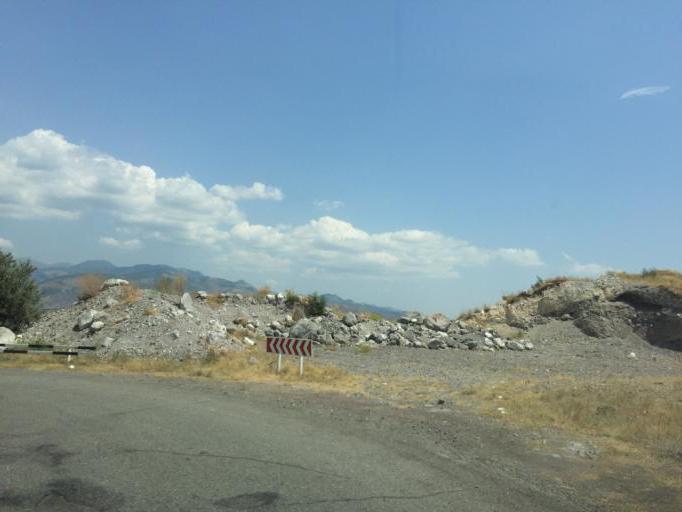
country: AZ
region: Lacin
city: Lacin
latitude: 39.5746
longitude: 46.5452
